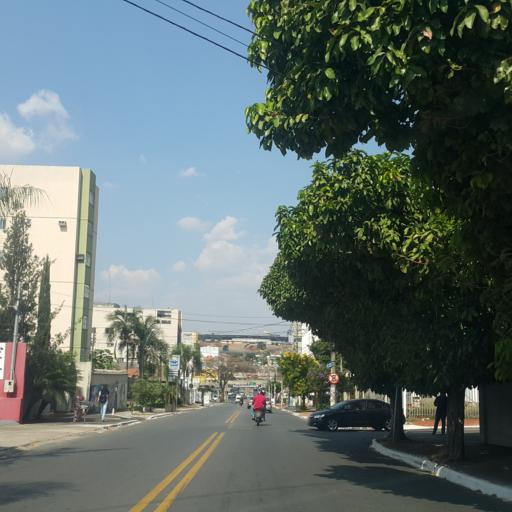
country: BR
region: Goias
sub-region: Goiania
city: Goiania
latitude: -16.6931
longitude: -49.2473
